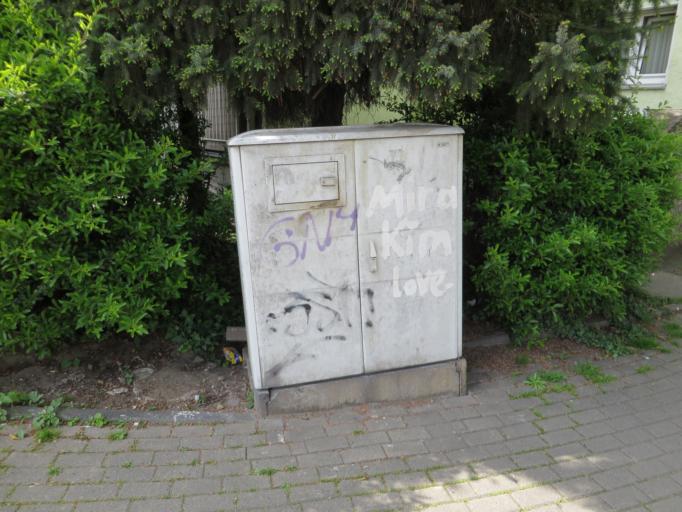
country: DE
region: North Rhine-Westphalia
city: Witten
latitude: 51.4468
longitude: 7.3234
